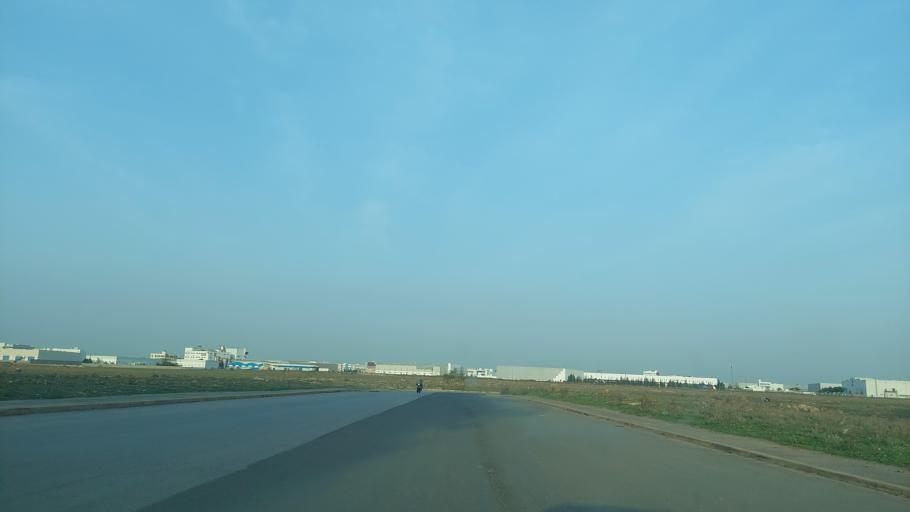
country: MA
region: Grand Casablanca
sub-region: Mediouna
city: Mediouna
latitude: 33.3949
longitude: -7.5516
